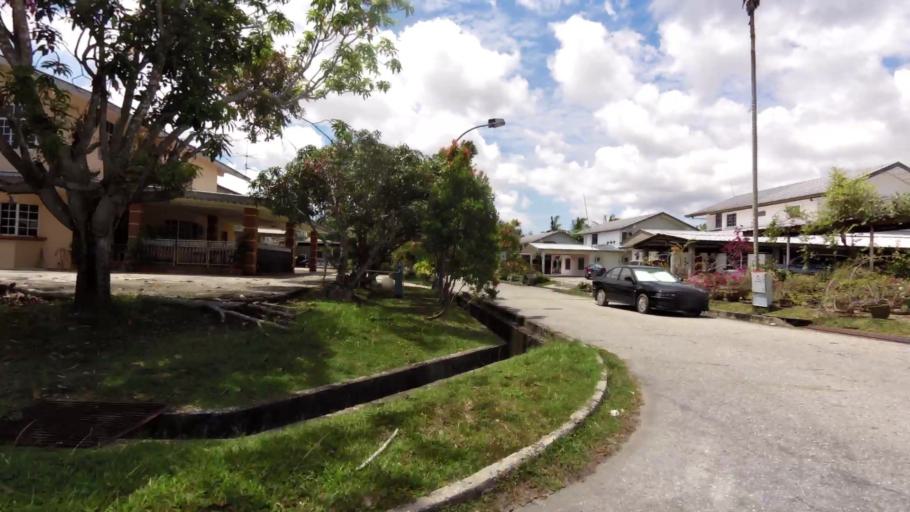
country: BN
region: Brunei and Muara
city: Bandar Seri Begawan
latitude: 4.9599
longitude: 114.8989
